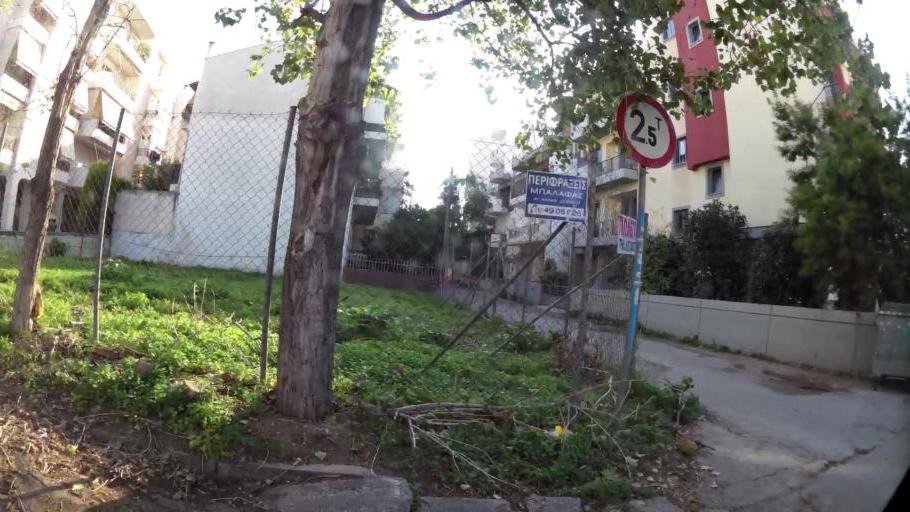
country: GR
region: Attica
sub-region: Nomarchia Anatolikis Attikis
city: Acharnes
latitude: 38.0640
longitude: 23.7375
